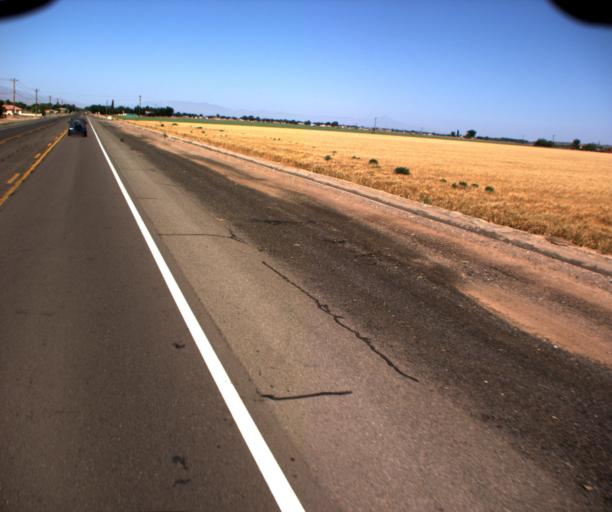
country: US
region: Arizona
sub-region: Graham County
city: Safford
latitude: 32.8167
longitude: -109.6618
